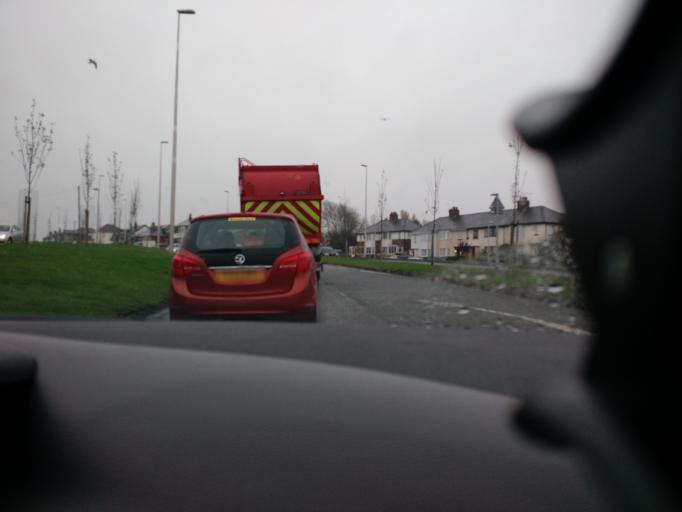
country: GB
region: England
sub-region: Lancashire
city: Great Marton
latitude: 53.8285
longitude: -3.0246
